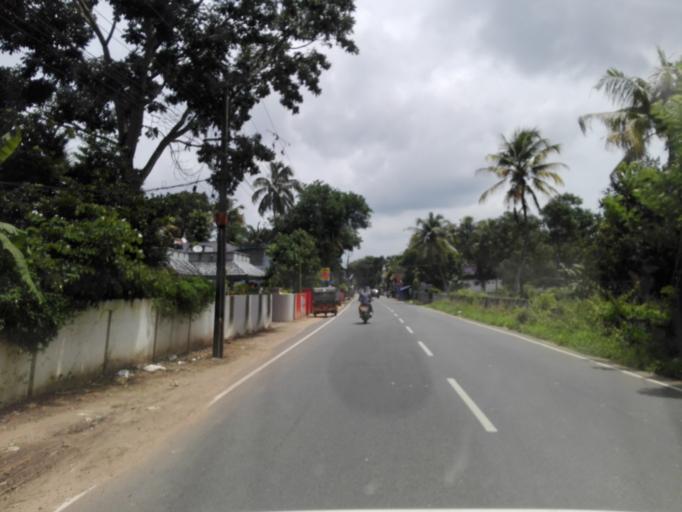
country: IN
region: Kerala
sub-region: Alappuzha
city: Arukutti
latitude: 9.8614
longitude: 76.3824
